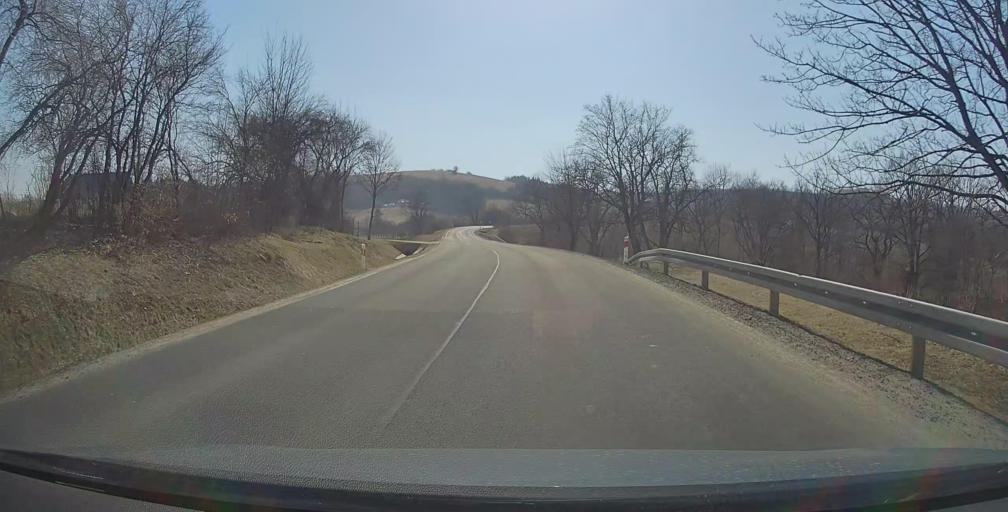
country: PL
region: Subcarpathian Voivodeship
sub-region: Powiat przemyski
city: Bircza
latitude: 49.6578
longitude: 22.4303
